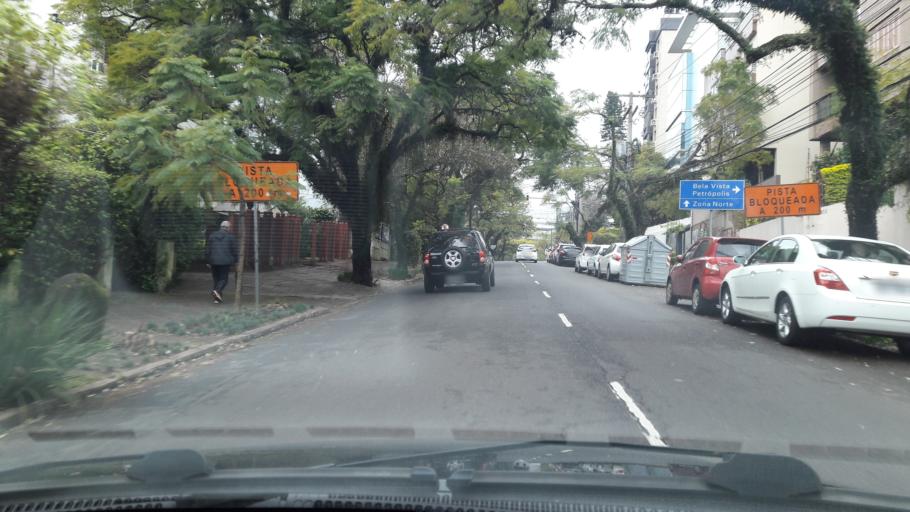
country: BR
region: Rio Grande do Sul
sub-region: Porto Alegre
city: Porto Alegre
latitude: -30.0267
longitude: -51.1880
